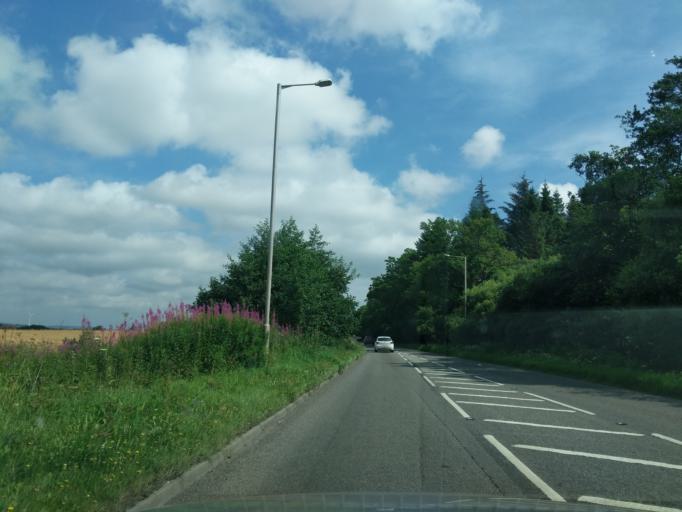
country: GB
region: Scotland
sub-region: Angus
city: Muirhead
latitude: 56.5048
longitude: -3.1311
